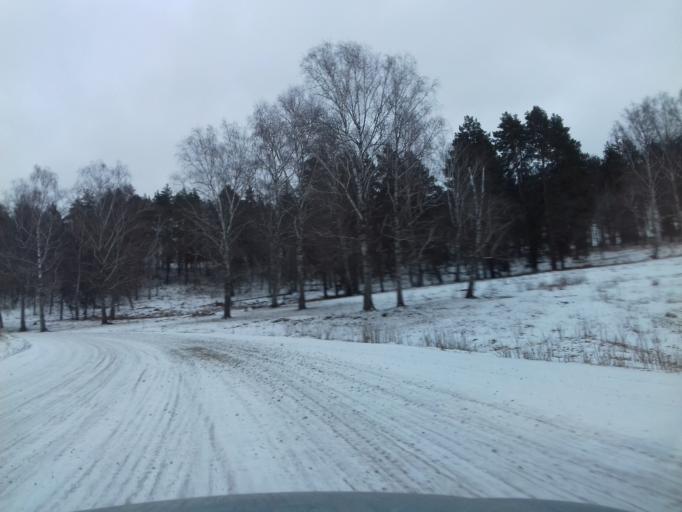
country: RU
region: Bashkortostan
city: Starosubkhangulovo
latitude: 53.0882
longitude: 57.4327
